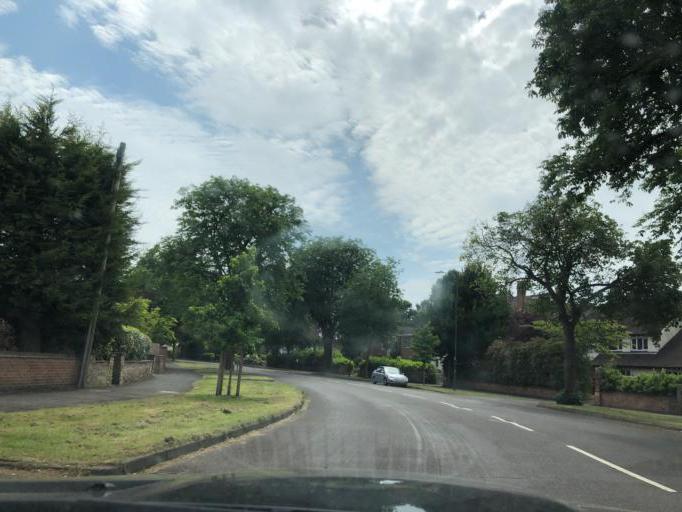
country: GB
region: England
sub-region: Warwickshire
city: Royal Leamington Spa
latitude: 52.3002
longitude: -1.5427
